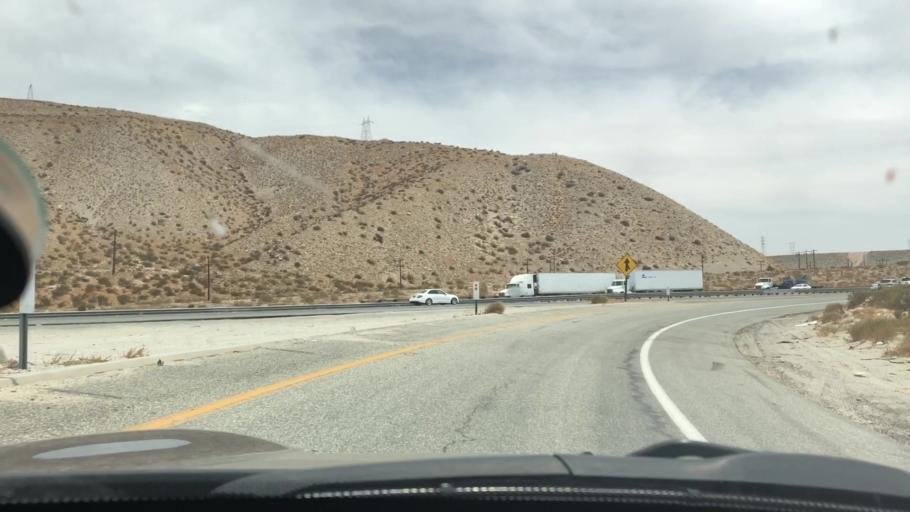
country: US
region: California
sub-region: Riverside County
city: Garnet
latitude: 33.9226
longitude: -116.6472
